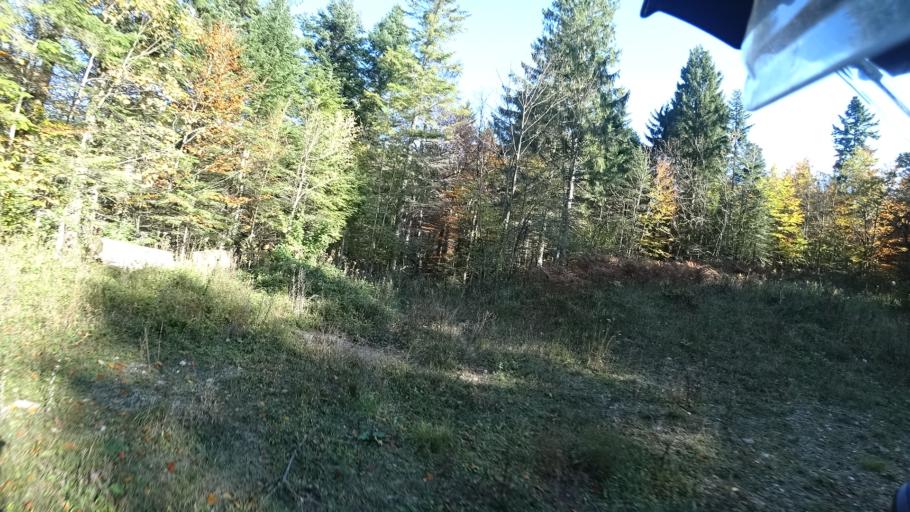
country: HR
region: Karlovacka
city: Plaski
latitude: 45.0332
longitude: 15.3539
